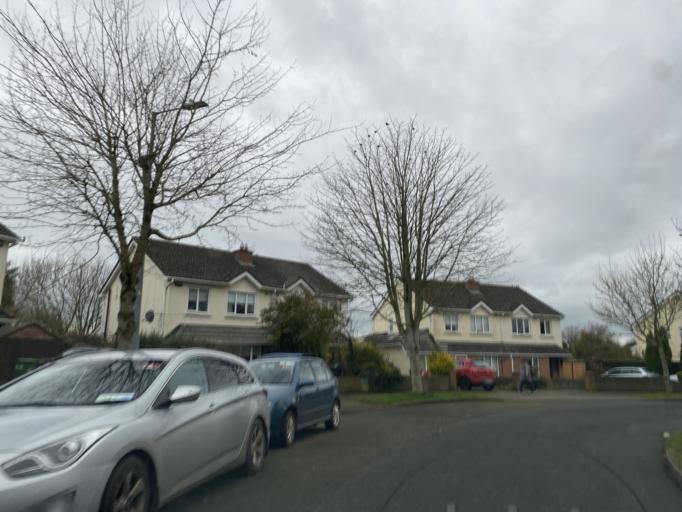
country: IE
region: Leinster
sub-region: Kildare
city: Celbridge
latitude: 53.3505
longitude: -6.5564
